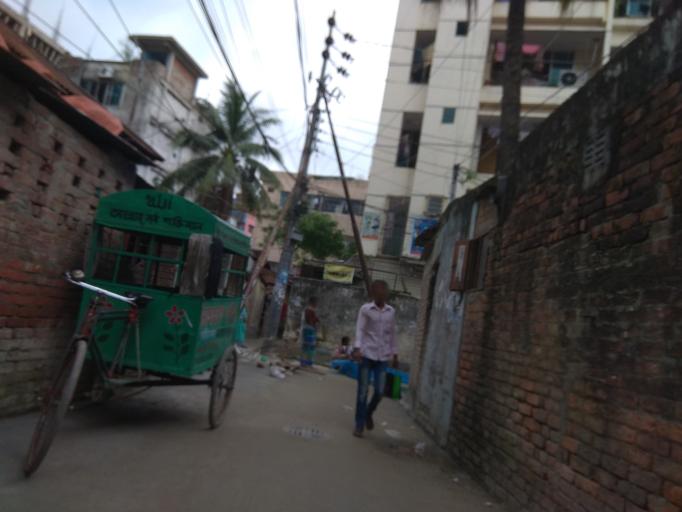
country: BD
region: Dhaka
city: Azimpur
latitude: 23.7933
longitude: 90.3839
